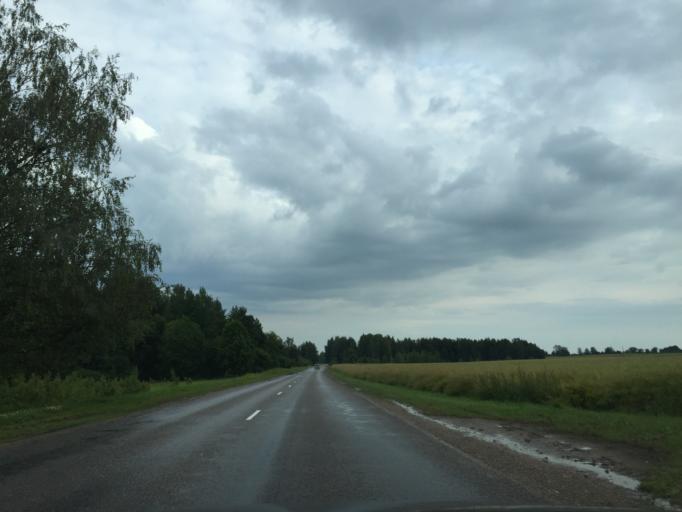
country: LV
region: Dobeles Rajons
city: Dobele
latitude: 56.6005
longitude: 23.2803
